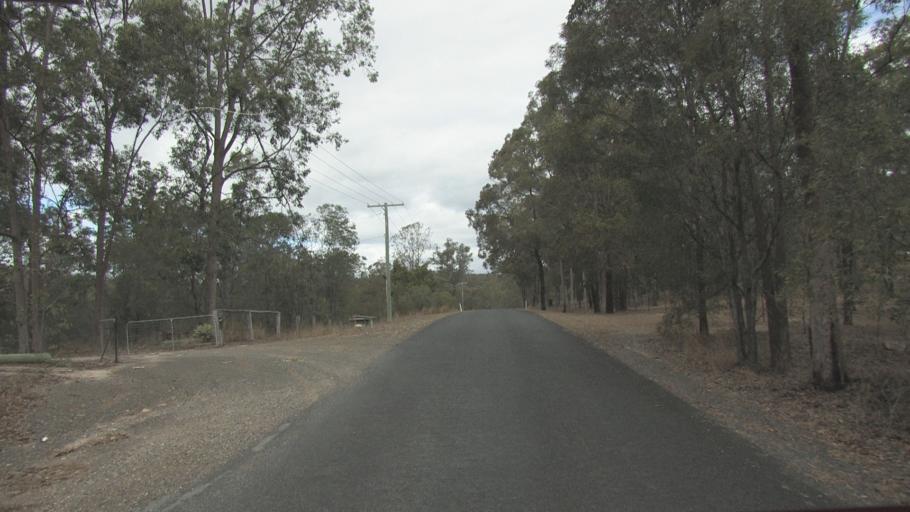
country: AU
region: Queensland
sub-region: Logan
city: Cedar Vale
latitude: -27.8844
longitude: 153.0337
